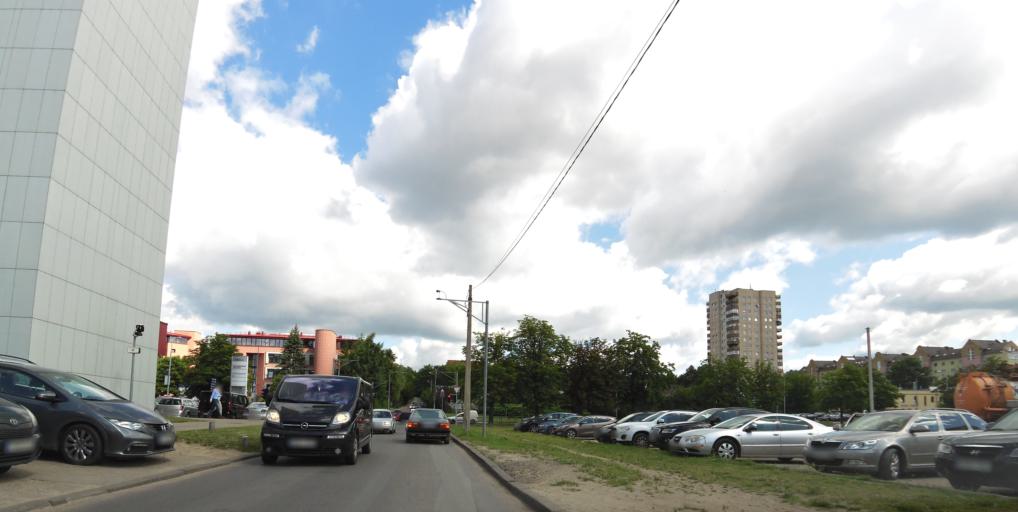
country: LT
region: Vilnius County
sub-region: Vilnius
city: Vilnius
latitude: 54.7034
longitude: 25.2798
